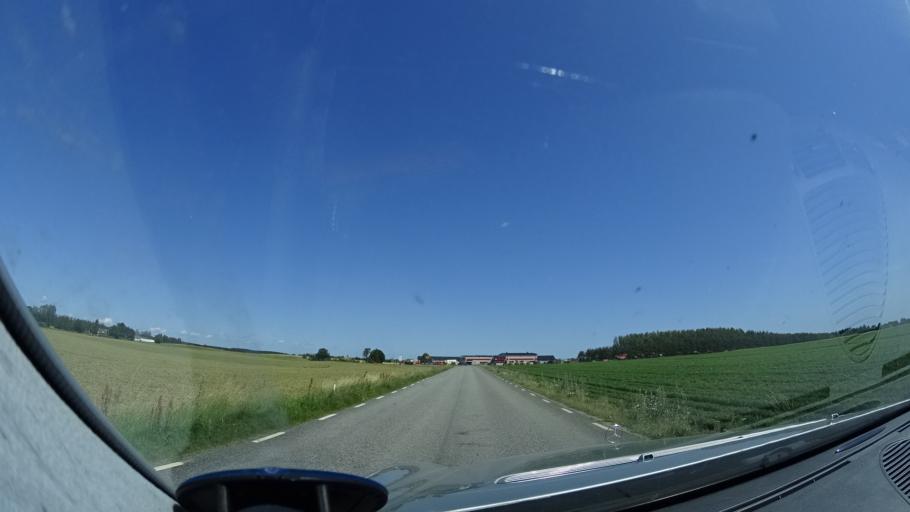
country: SE
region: Skane
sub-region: Kristianstads Kommun
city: Degeberga
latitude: 55.8903
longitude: 14.0370
